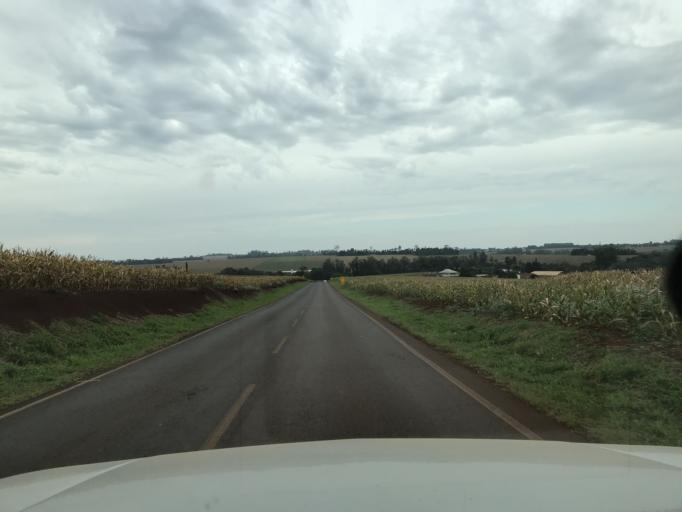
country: BR
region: Parana
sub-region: Palotina
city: Palotina
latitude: -24.4432
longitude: -53.9178
